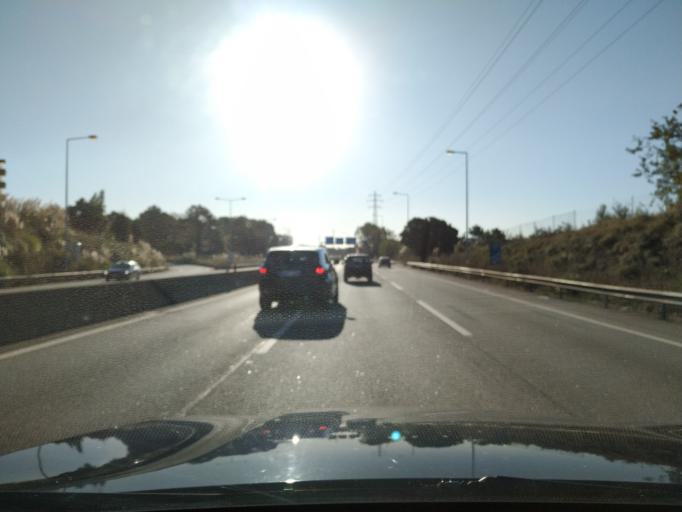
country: PT
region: Porto
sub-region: Vila Nova de Gaia
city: Canidelo
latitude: 41.1181
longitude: -8.6328
